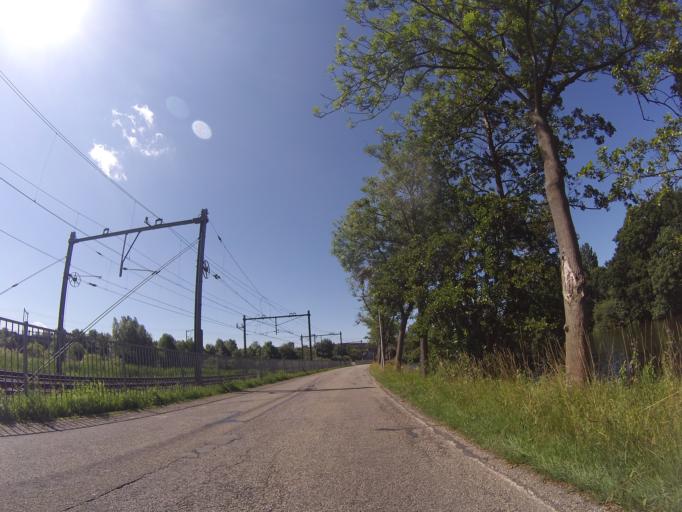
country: NL
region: Utrecht
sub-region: Gemeente Utrecht
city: Utrecht
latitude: 52.1149
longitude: 5.1413
